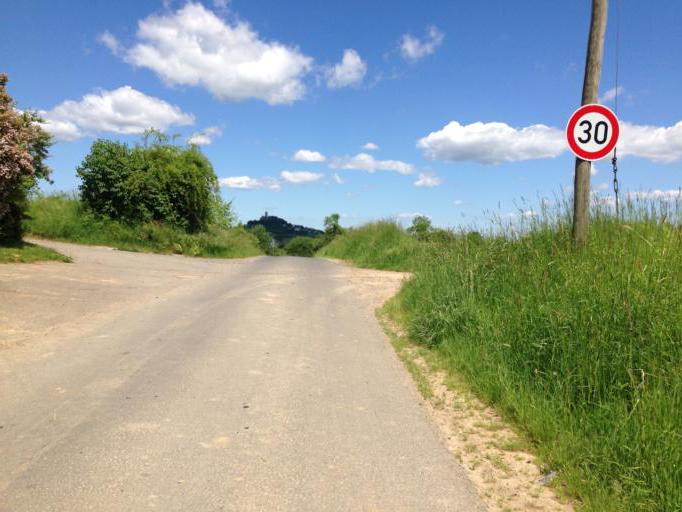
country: DE
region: Hesse
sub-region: Regierungsbezirk Giessen
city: Heuchelheim
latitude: 50.5944
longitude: 8.6097
